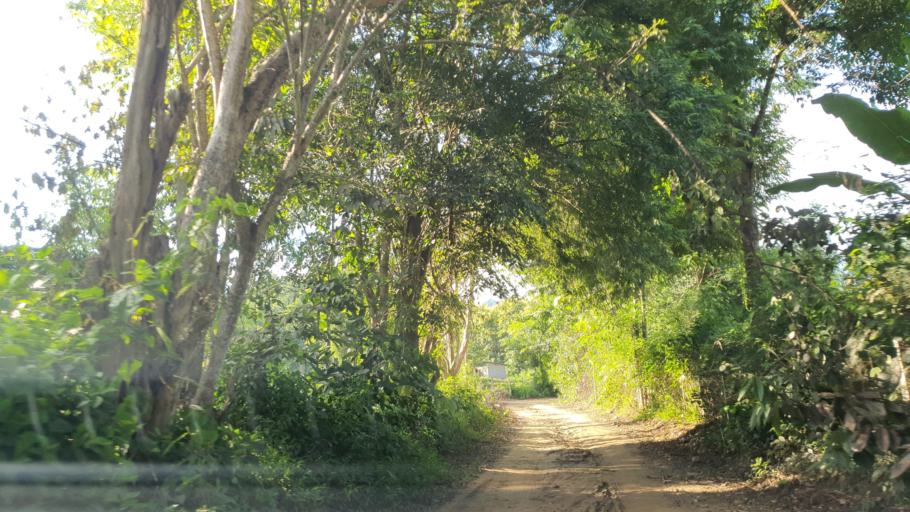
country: TH
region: Chiang Mai
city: Hang Dong
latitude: 18.7162
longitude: 98.8533
